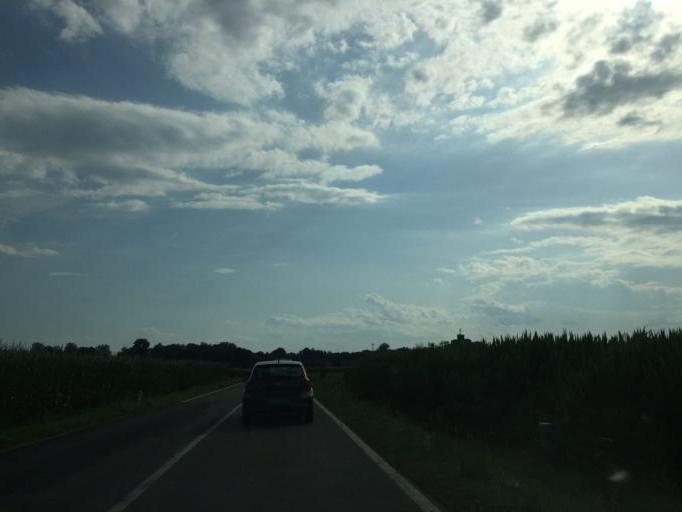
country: AT
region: Styria
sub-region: Politischer Bezirk Suedoststeiermark
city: Deutsch Goritz
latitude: 46.7317
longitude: 15.8594
